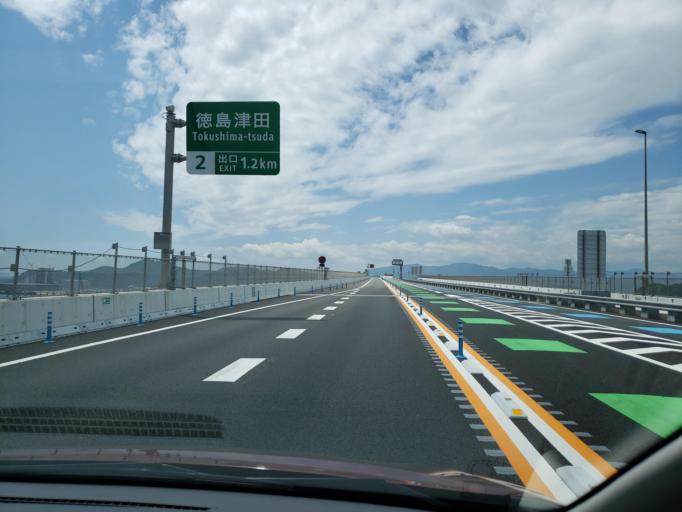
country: JP
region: Tokushima
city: Tokushima-shi
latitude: 34.0591
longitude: 134.5904
